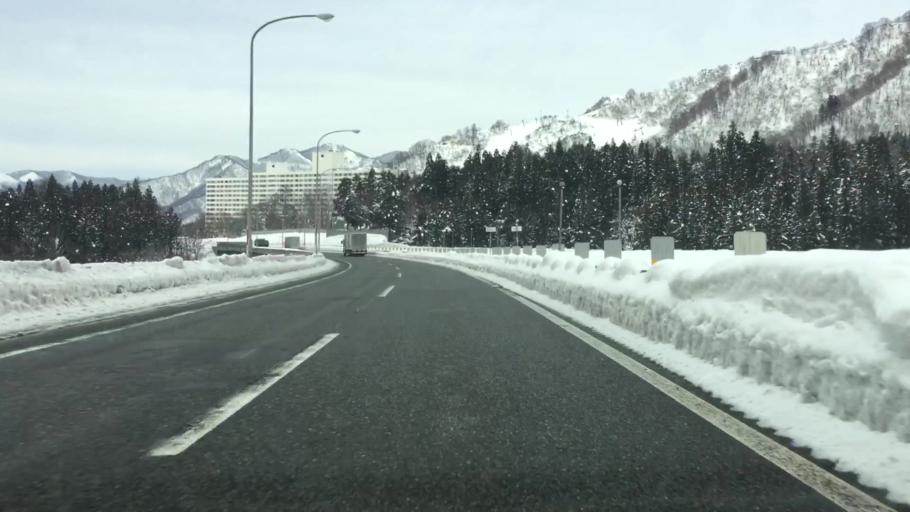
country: JP
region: Niigata
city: Shiozawa
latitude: 36.8999
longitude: 138.8469
